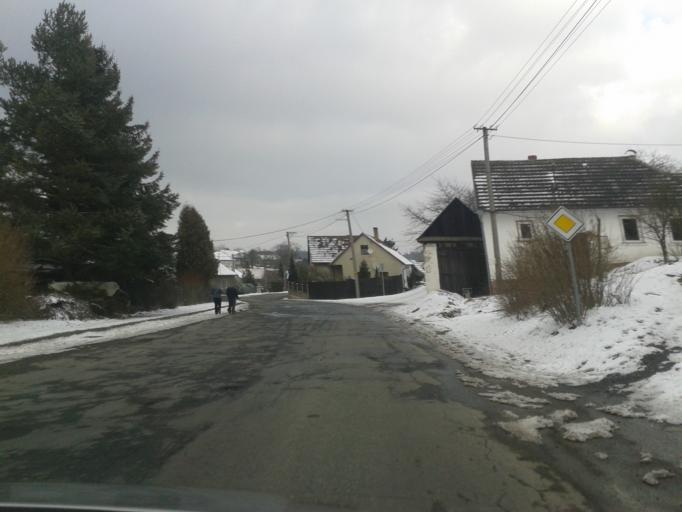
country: CZ
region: Olomoucky
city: Horni Stepanov
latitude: 49.5505
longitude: 16.7911
